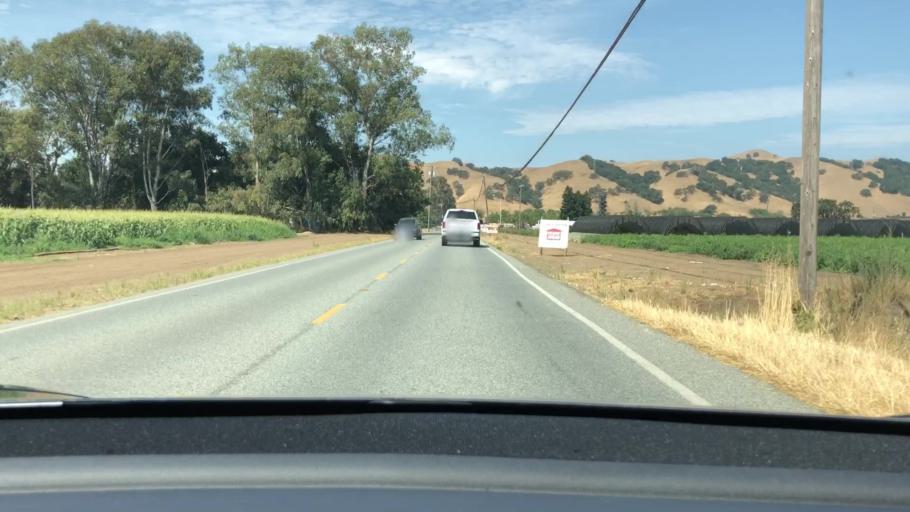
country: US
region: California
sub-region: Santa Clara County
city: San Martin
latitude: 37.0549
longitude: -121.5995
